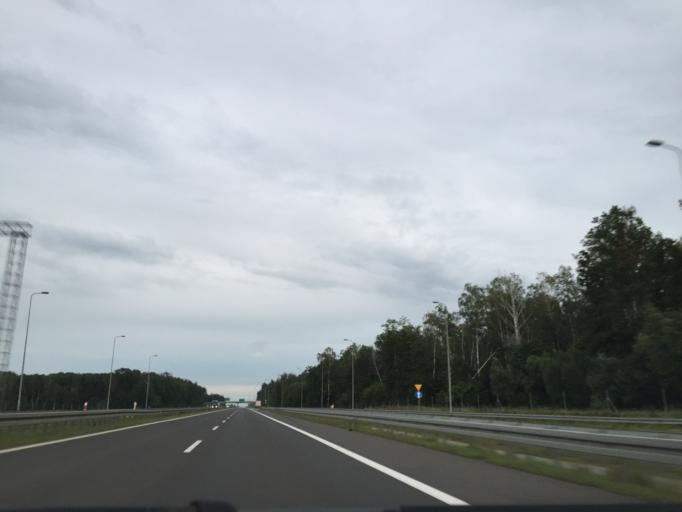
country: PL
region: Podlasie
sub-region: Powiat bialostocki
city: Tykocin
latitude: 53.1367
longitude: 22.7526
